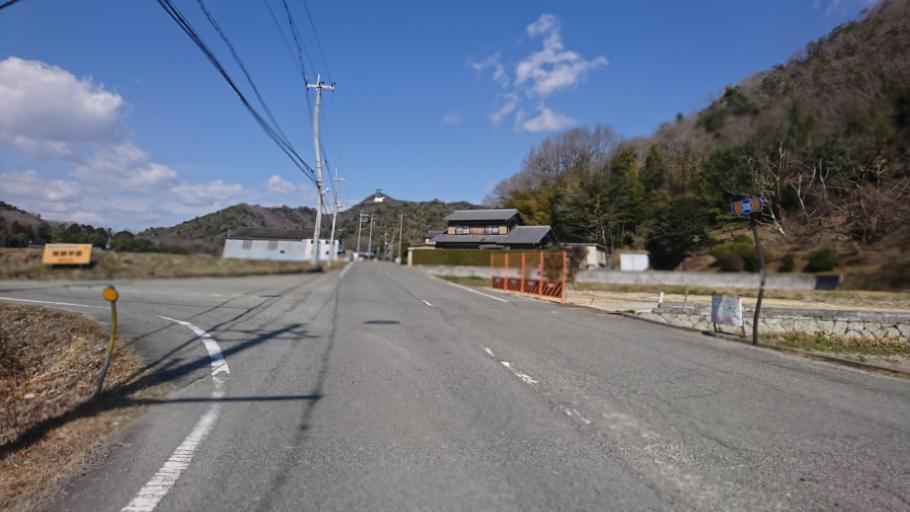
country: JP
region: Hyogo
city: Kakogawacho-honmachi
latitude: 34.8511
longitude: 134.8105
